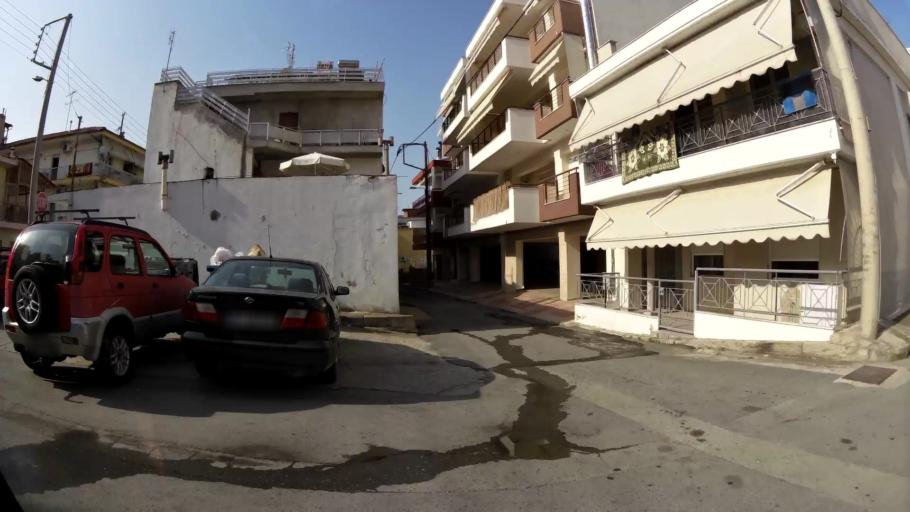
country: GR
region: Central Macedonia
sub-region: Nomos Thessalonikis
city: Evosmos
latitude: 40.6655
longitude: 22.9184
